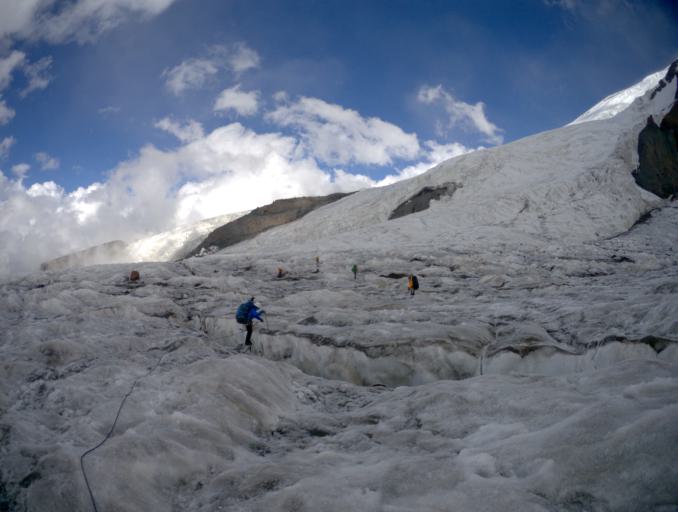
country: RU
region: Kabardino-Balkariya
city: Terskol
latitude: 43.3858
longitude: 42.4255
